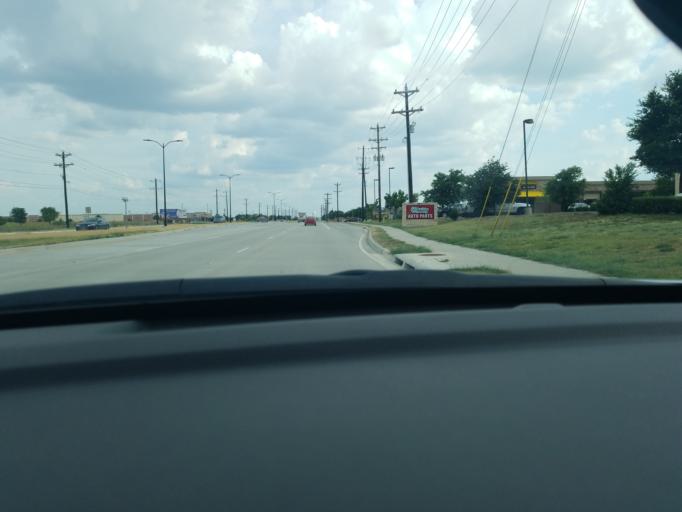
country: US
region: Texas
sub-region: Denton County
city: Little Elm
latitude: 33.1857
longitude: -96.8872
